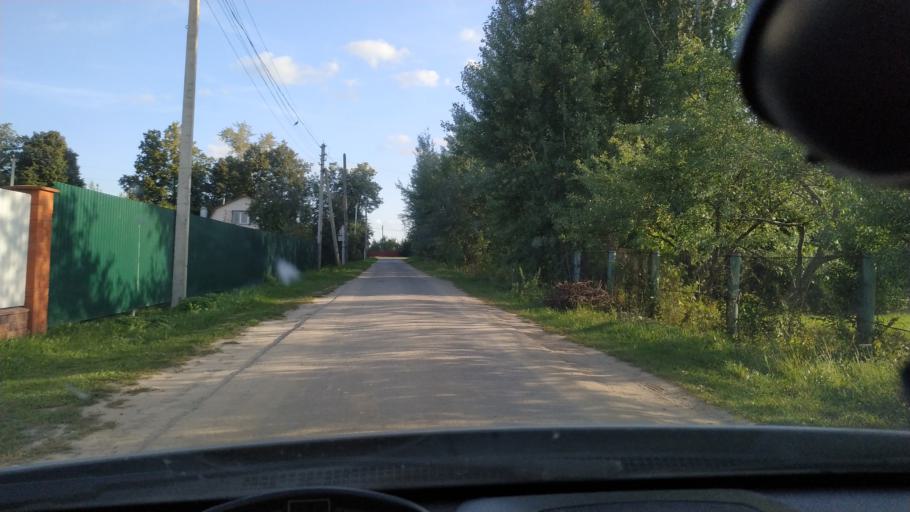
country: RU
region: Rjazan
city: Solotcha
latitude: 54.8673
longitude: 39.6697
